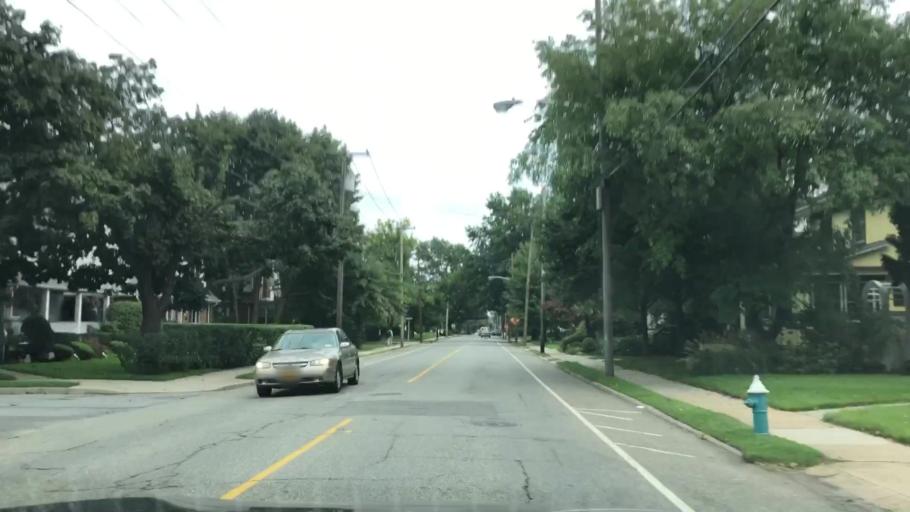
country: US
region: New York
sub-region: Nassau County
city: Floral Park
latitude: 40.7229
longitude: -73.7001
